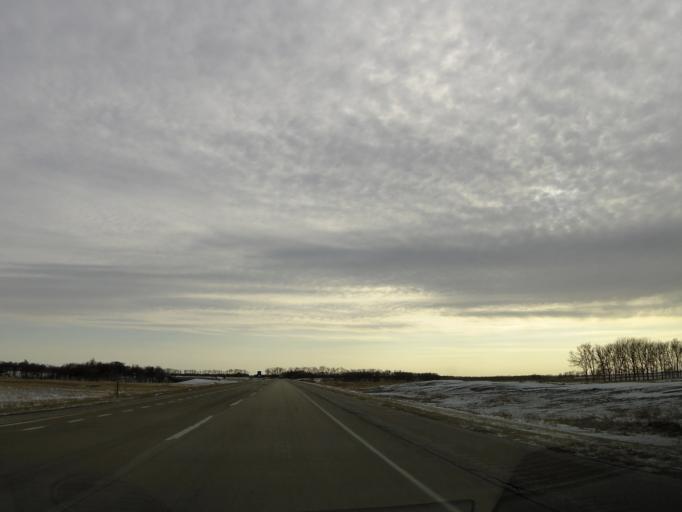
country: US
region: North Dakota
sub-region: Walsh County
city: Grafton
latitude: 48.4641
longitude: -97.1929
